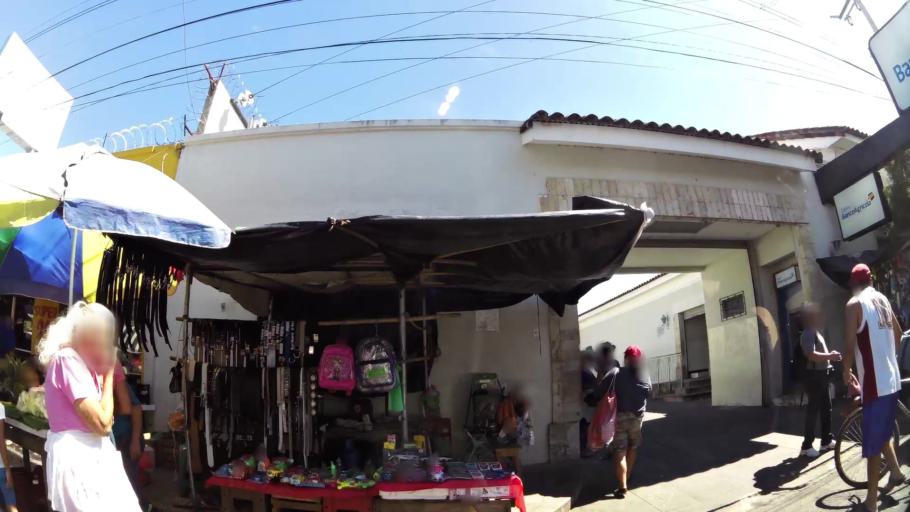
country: SV
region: La Libertad
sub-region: Distrito de Quezaltepeque
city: Quezaltepeque
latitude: 13.8347
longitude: -89.2723
